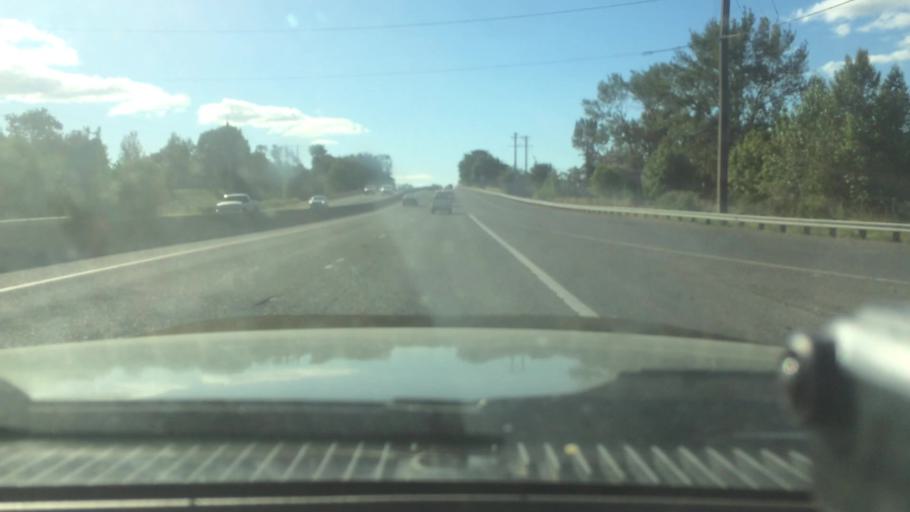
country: US
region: Oregon
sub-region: Lane County
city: Eugene
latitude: 44.0934
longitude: -123.1030
